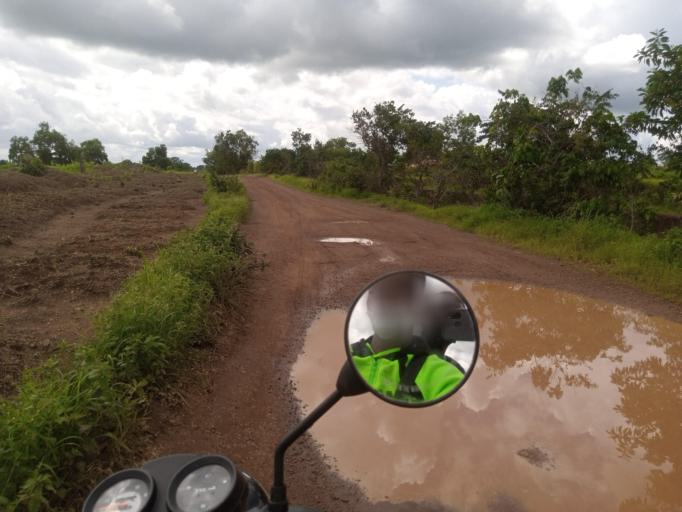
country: SL
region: Northern Province
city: Port Loko
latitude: 8.7703
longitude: -12.7737
